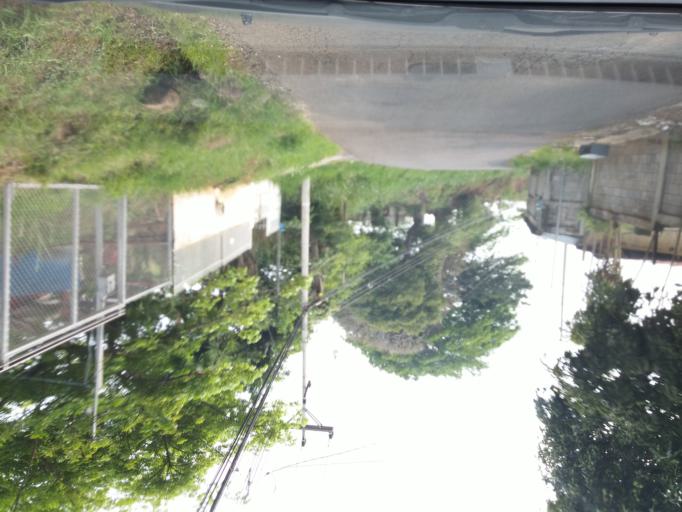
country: CR
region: Alajuela
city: Alajuela
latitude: 9.9899
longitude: -84.2293
